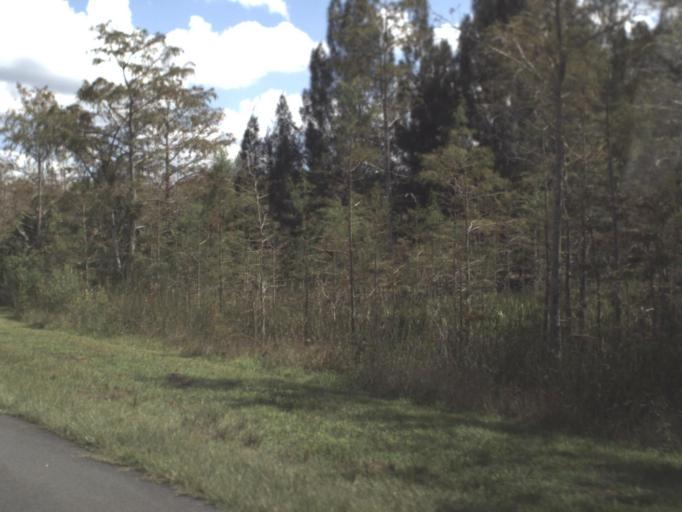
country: US
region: Florida
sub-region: Miami-Dade County
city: Kendall West
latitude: 25.8471
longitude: -80.9365
